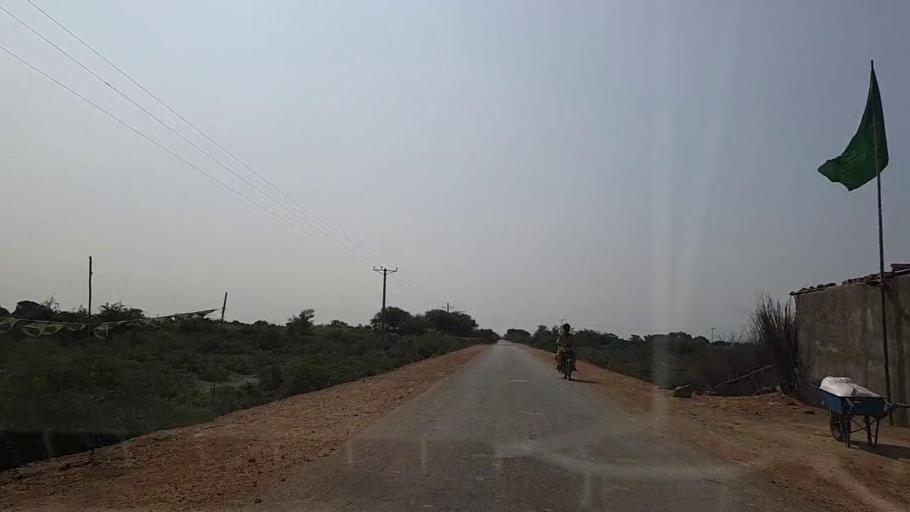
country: PK
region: Sindh
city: Chuhar Jamali
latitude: 24.2767
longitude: 67.9168
